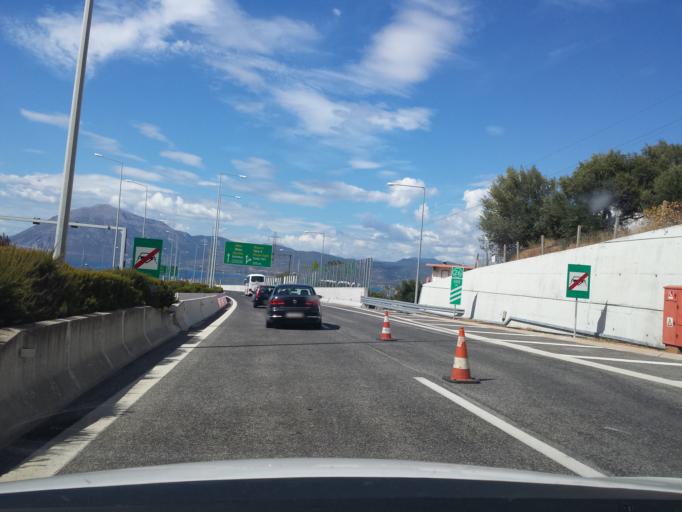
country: GR
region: West Greece
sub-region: Nomos Achaias
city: Rio
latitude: 38.2795
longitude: 21.7824
